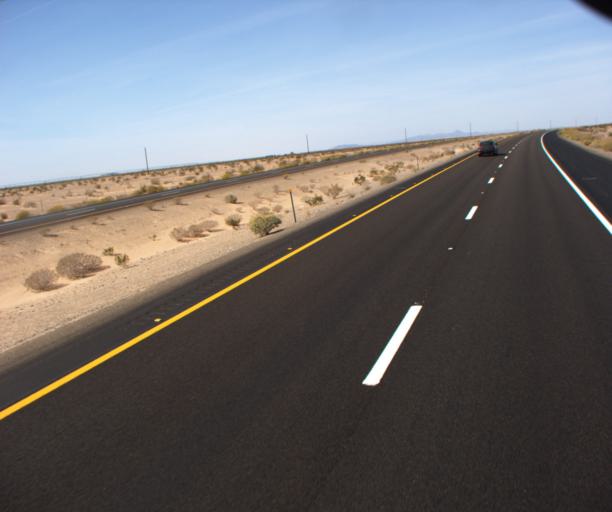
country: US
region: Arizona
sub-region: Yuma County
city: Somerton
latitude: 32.5111
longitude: -114.5595
